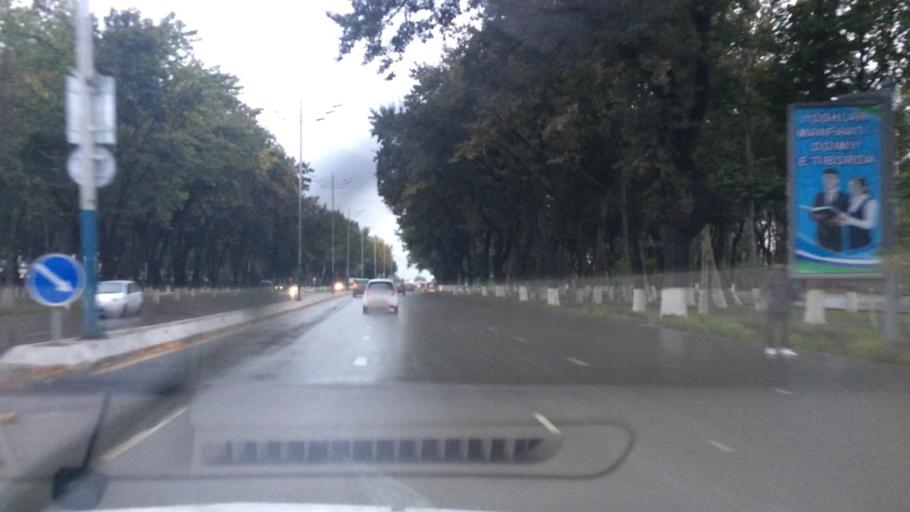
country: UZ
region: Toshkent Shahri
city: Tashkent
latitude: 41.2978
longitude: 69.2296
